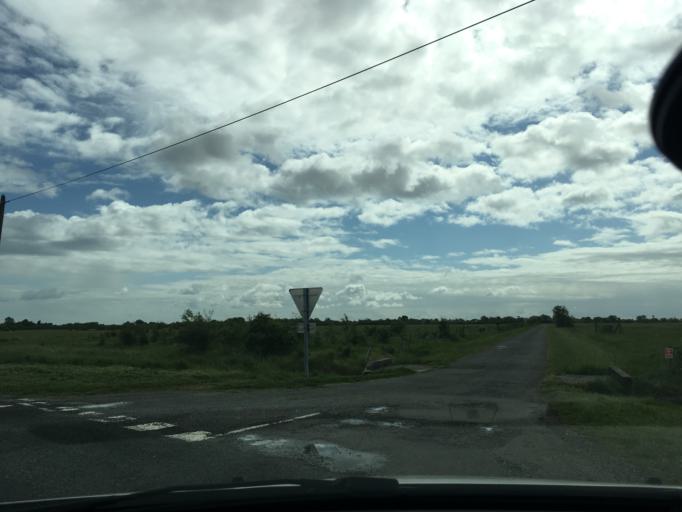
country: FR
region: Aquitaine
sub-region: Departement de la Gironde
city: Saint-Estephe
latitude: 45.3327
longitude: -0.8101
